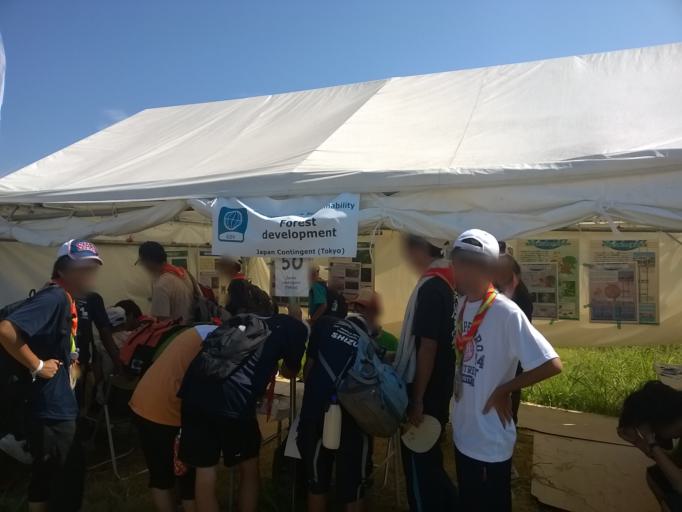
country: JP
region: Yamaguchi
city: Ogori-shimogo
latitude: 34.0155
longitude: 131.3694
